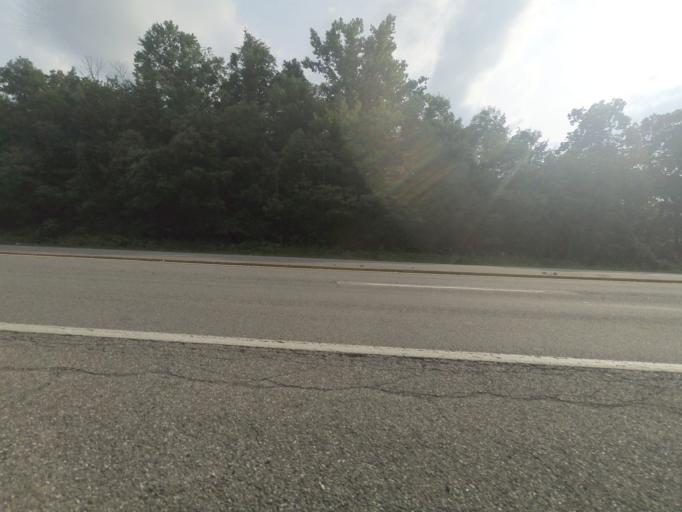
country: US
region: West Virginia
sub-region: Cabell County
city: Huntington
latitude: 38.3997
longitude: -82.4234
